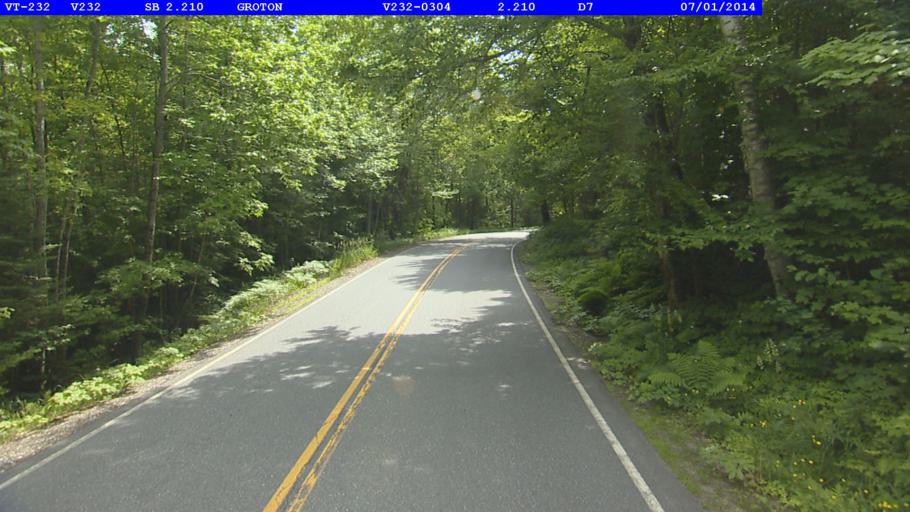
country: US
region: New Hampshire
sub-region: Grafton County
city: Woodsville
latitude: 44.2438
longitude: -72.2488
